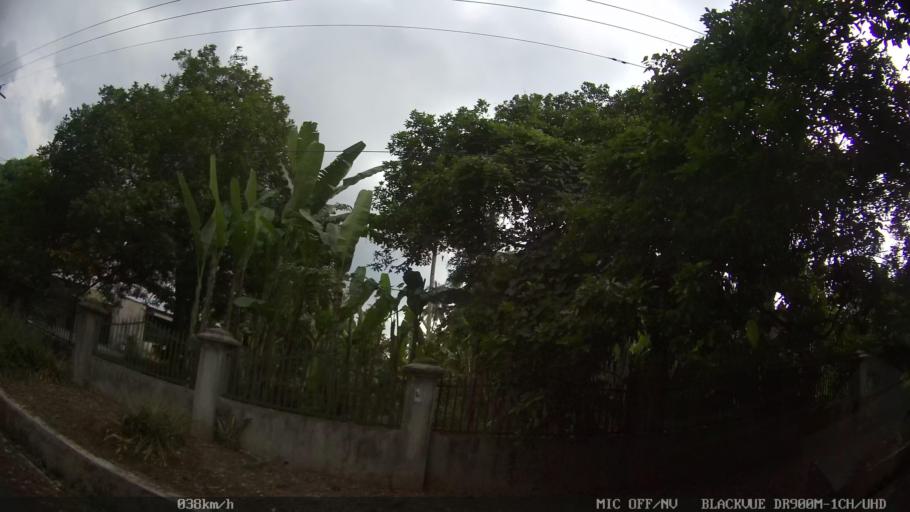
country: ID
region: North Sumatra
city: Sunggal
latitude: 3.5294
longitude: 98.6078
